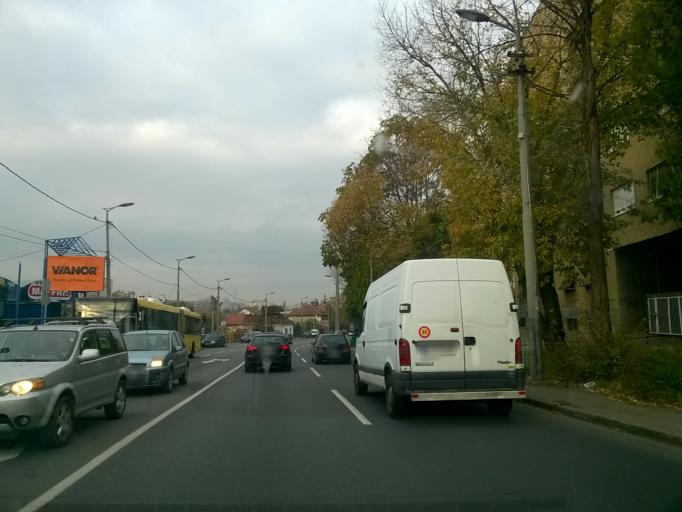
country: RS
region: Central Serbia
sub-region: Belgrade
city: Vozdovac
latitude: 44.7844
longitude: 20.4857
